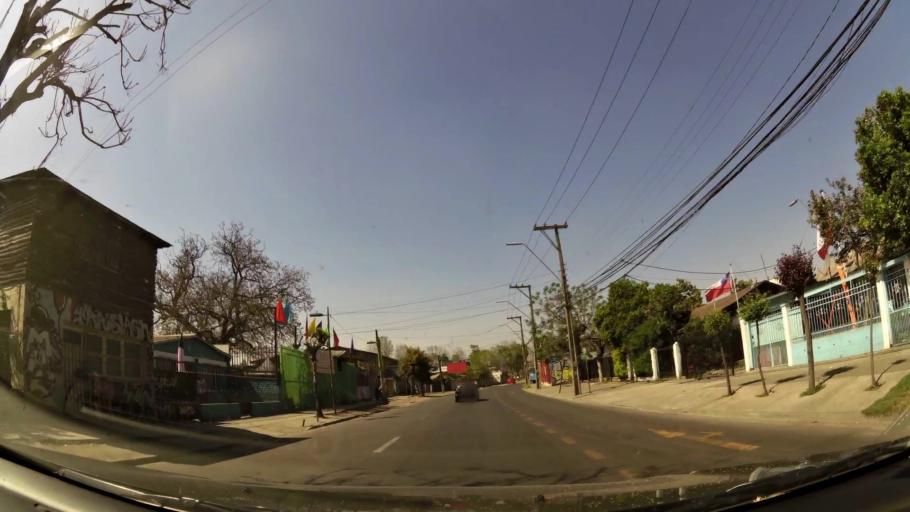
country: CL
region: Santiago Metropolitan
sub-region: Provincia de Santiago
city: Lo Prado
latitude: -33.4044
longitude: -70.7073
